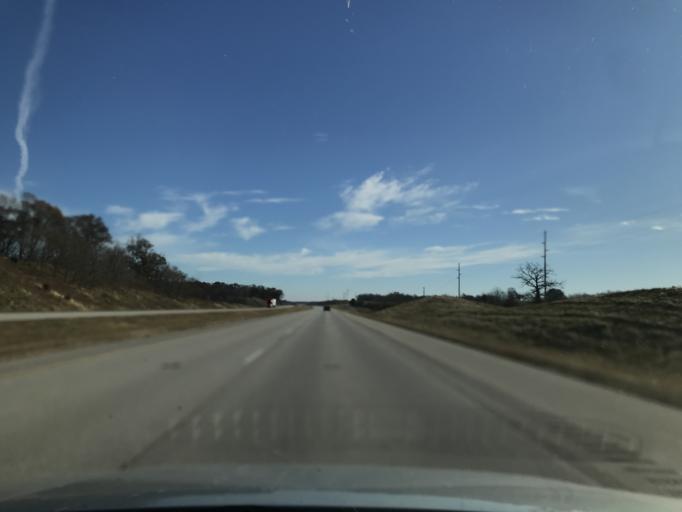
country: US
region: Illinois
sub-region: Hancock County
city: Carthage
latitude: 40.4143
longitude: -91.0304
